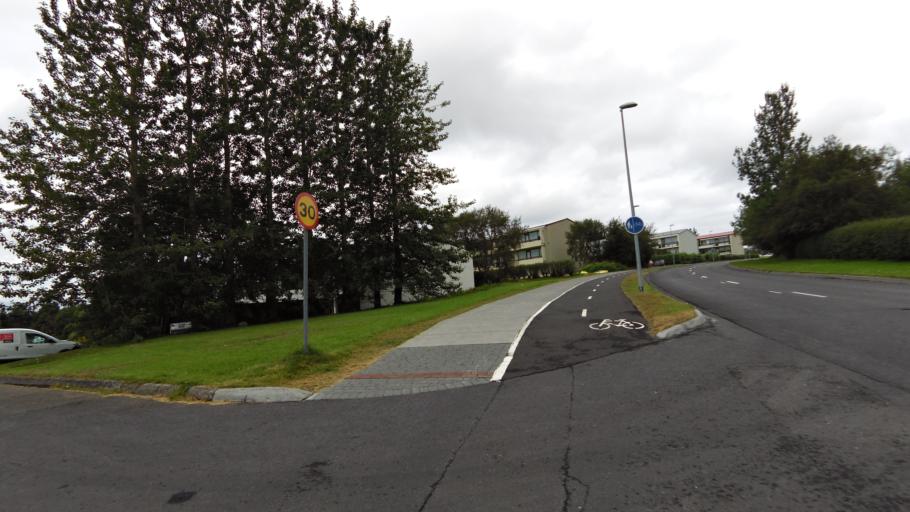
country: IS
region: Capital Region
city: Reykjavik
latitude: 64.1186
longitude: -21.8529
